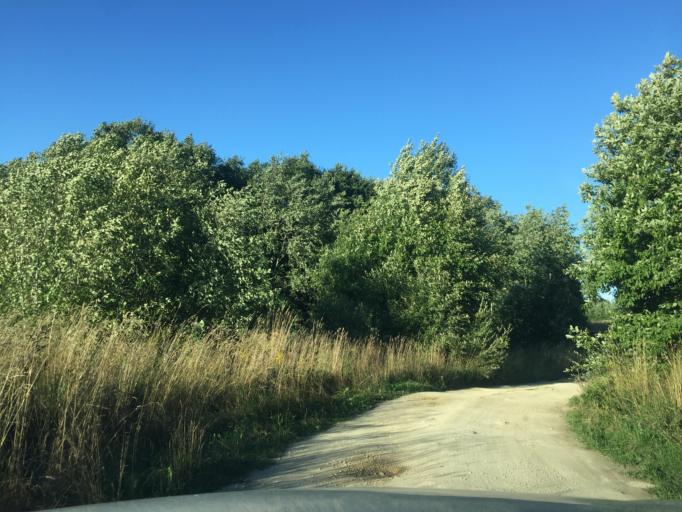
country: RU
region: Leningrad
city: Rozhdestveno
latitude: 59.3283
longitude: 29.9955
